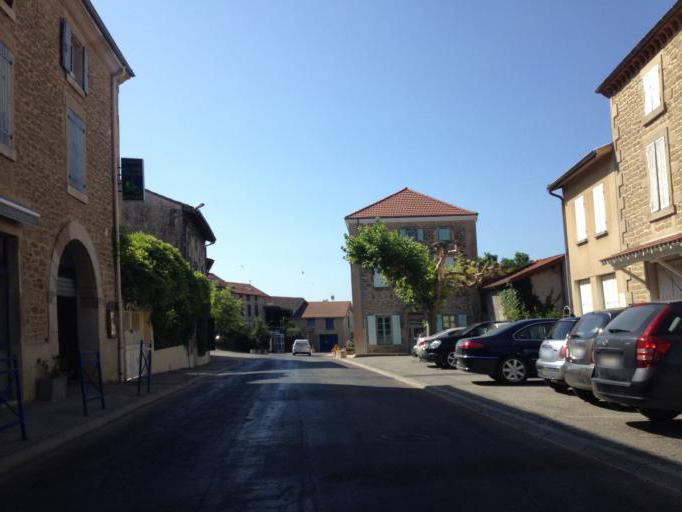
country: FR
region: Rhone-Alpes
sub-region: Departement de la Drome
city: Clerieux
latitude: 45.1358
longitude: 4.9479
